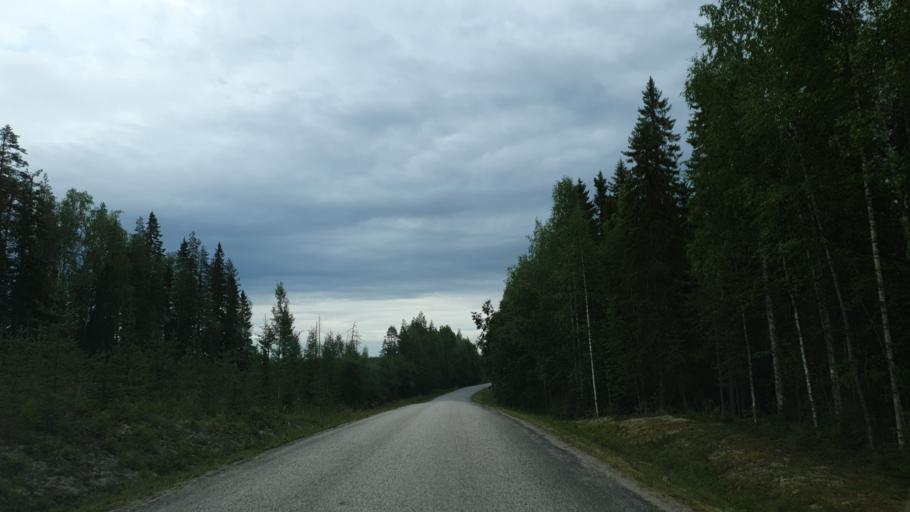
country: FI
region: Kainuu
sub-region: Kehys-Kainuu
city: Kuhmo
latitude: 64.3398
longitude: 29.3690
